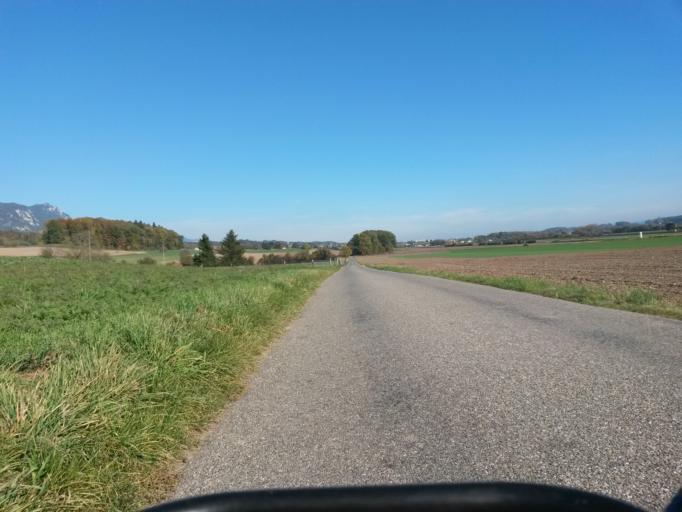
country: CH
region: Solothurn
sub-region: Bezirk Lebern
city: Selzach
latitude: 47.2065
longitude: 7.4653
